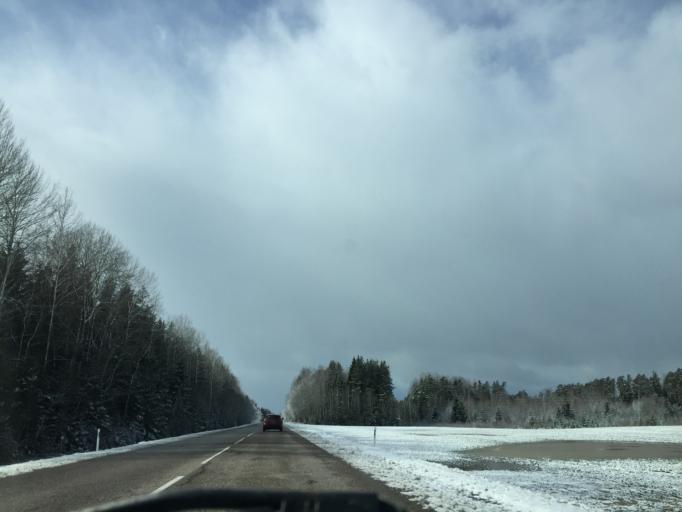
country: LV
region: Talsu Rajons
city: Stende
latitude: 57.2076
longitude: 22.4579
